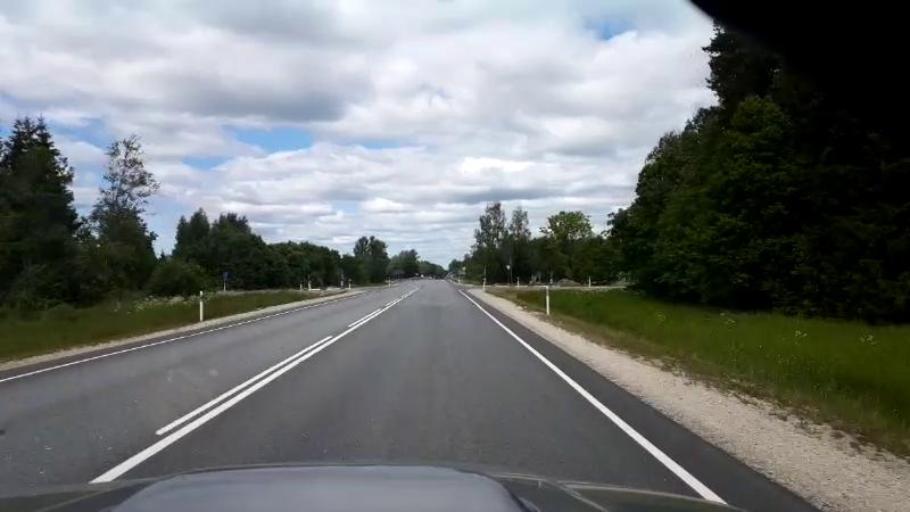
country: EE
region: Raplamaa
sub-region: Maerjamaa vald
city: Marjamaa
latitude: 58.8079
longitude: 24.4126
